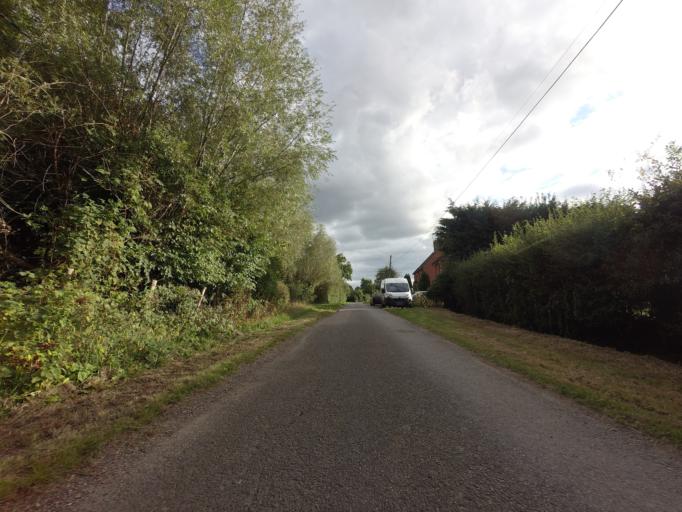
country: GB
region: England
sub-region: Kent
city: Staplehurst
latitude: 51.1951
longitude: 0.5729
